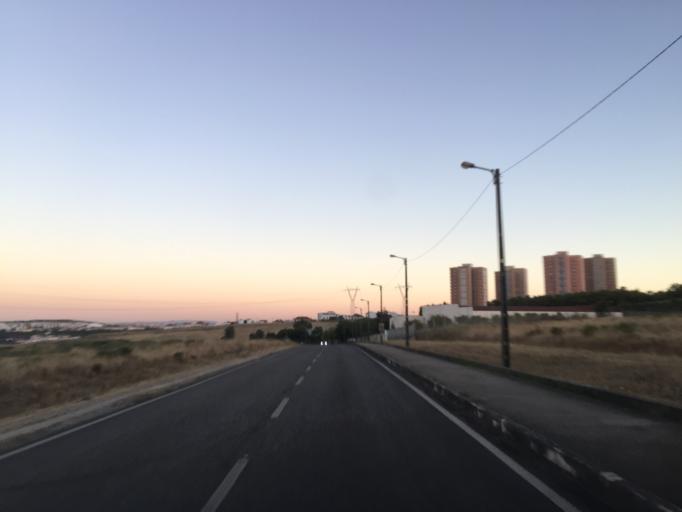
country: PT
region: Lisbon
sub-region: Odivelas
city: Povoa de Santo Adriao
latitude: 38.8142
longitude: -9.1752
